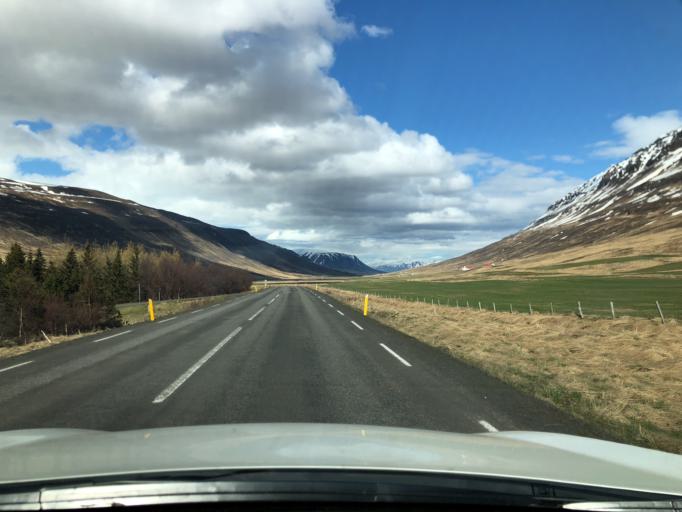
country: IS
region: Northeast
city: Dalvik
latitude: 65.6034
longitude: -18.5092
